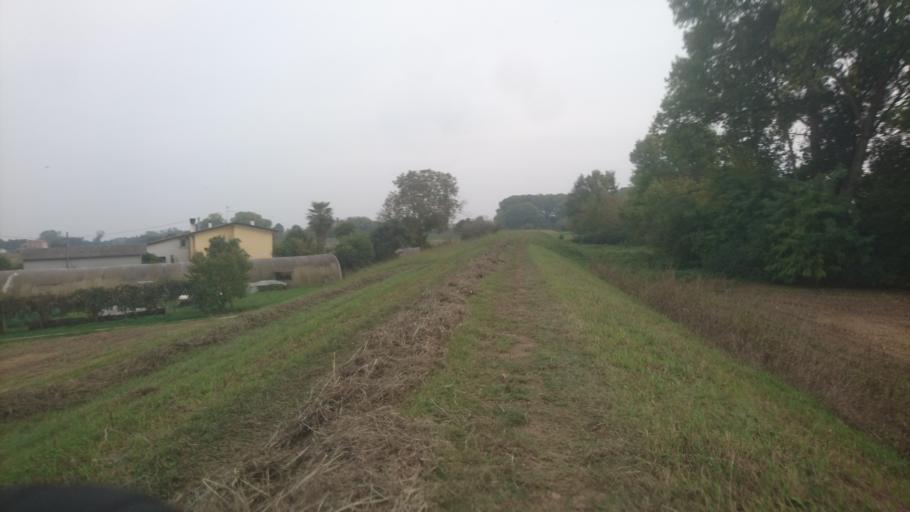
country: IT
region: Veneto
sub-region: Provincia di Padova
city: Cervarese Santa Croce
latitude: 45.4200
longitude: 11.7094
